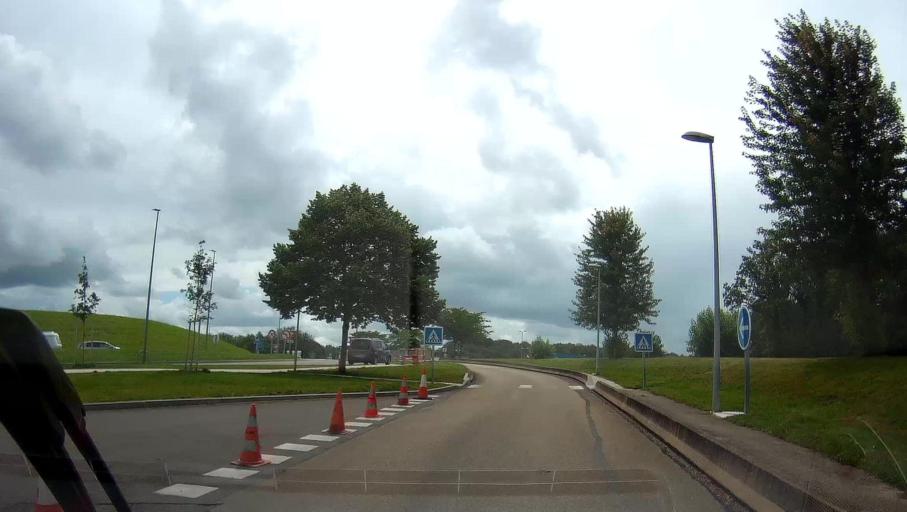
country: FR
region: Champagne-Ardenne
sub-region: Departement de la Haute-Marne
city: Langres
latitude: 47.8142
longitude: 5.2221
